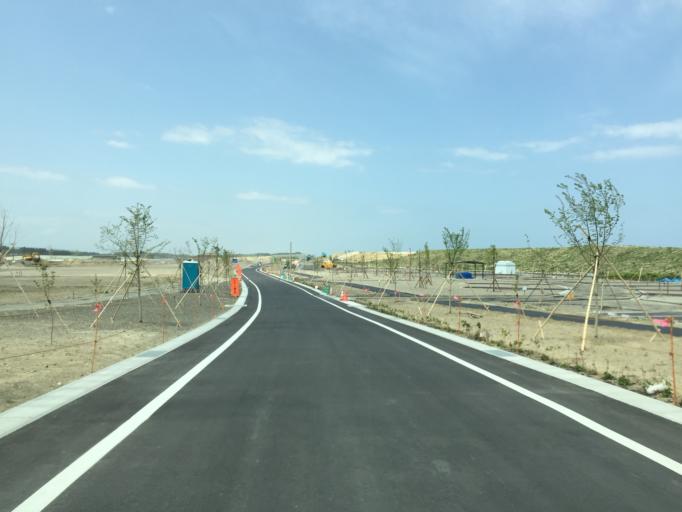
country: JP
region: Miyagi
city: Marumori
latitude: 37.8740
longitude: 140.9335
